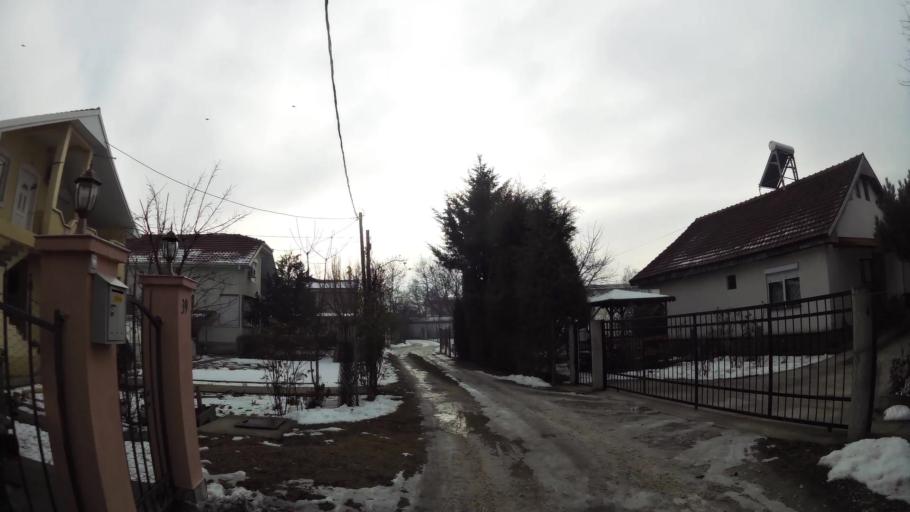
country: MK
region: Ilinden
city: Ilinden
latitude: 41.9937
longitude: 21.5827
